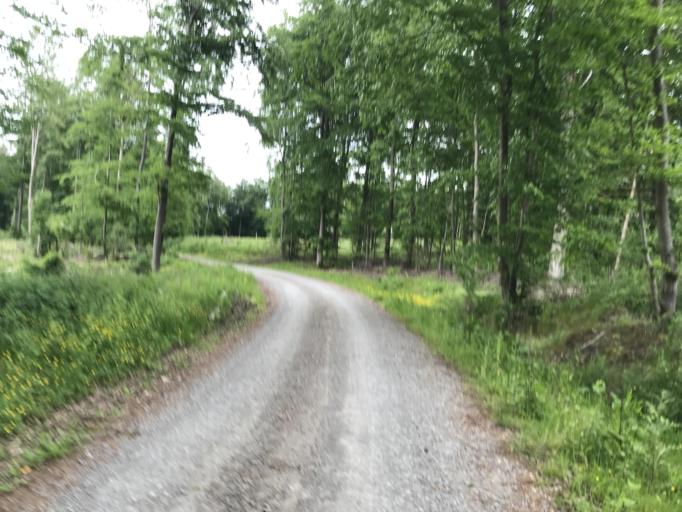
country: DE
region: Hesse
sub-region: Regierungsbezirk Kassel
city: Martinhagen
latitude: 51.2931
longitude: 9.2672
